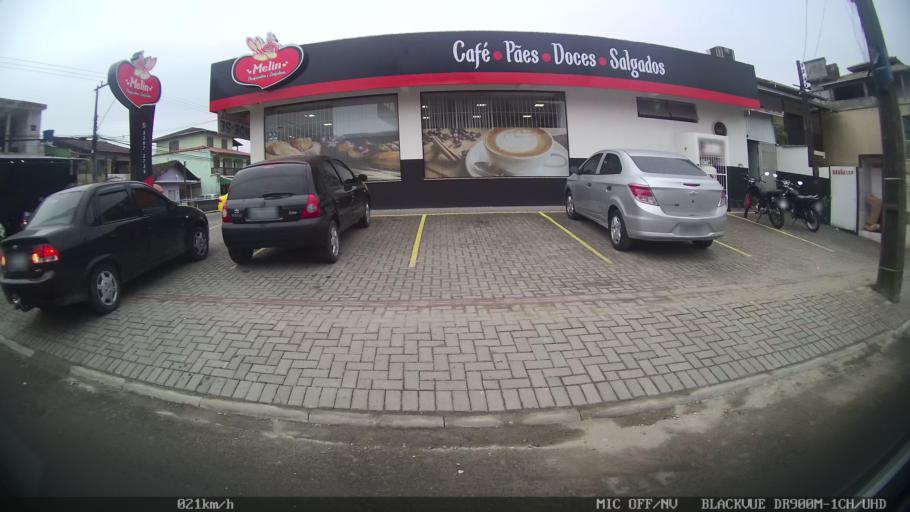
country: BR
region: Santa Catarina
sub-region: Joinville
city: Joinville
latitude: -26.2592
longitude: -48.8081
